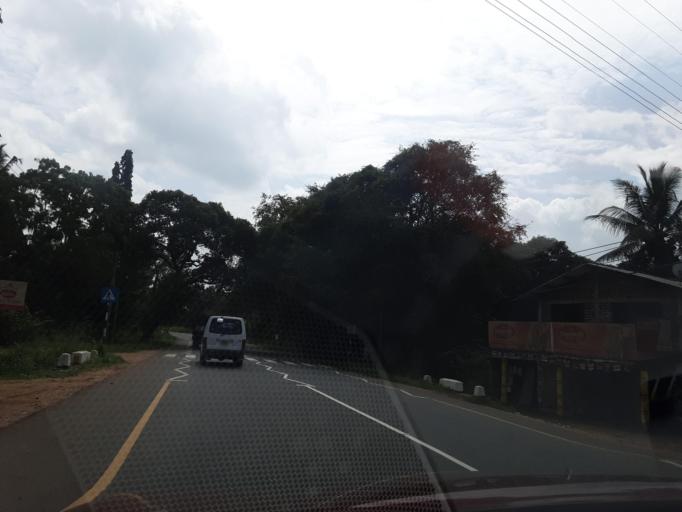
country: LK
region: North Central
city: Anuradhapura
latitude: 8.4857
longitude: 80.5105
